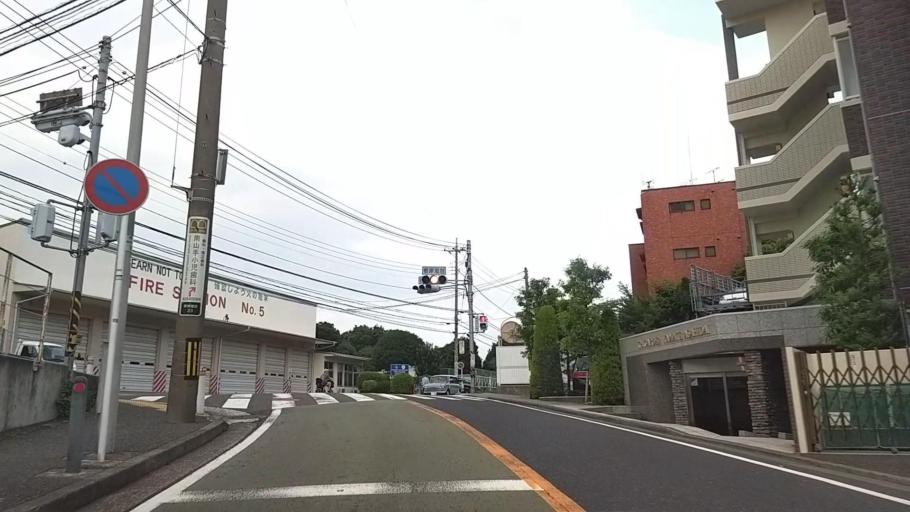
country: JP
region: Kanagawa
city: Yokohama
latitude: 35.4201
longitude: 139.6373
